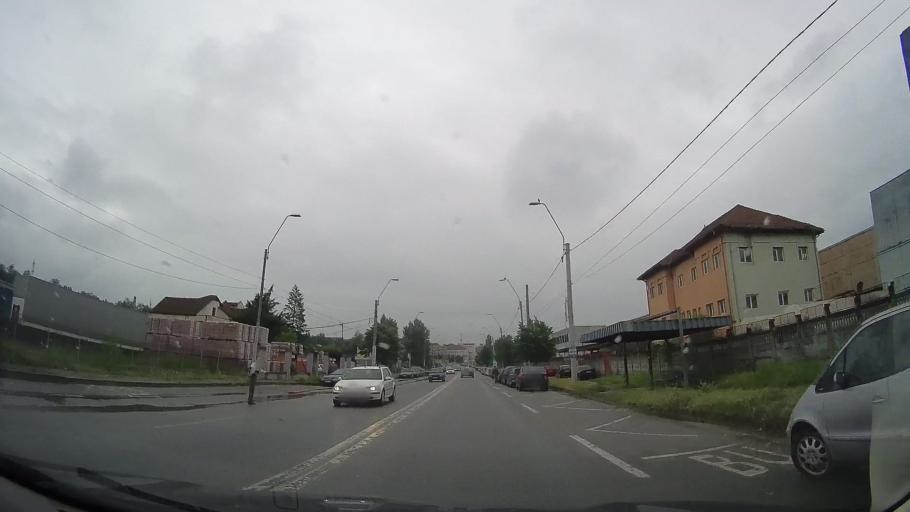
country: RO
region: Mehedinti
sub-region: Municipiul Drobeta-Turnu Severin
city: Drobeta-Turnu Severin
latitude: 44.6239
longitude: 22.6337
